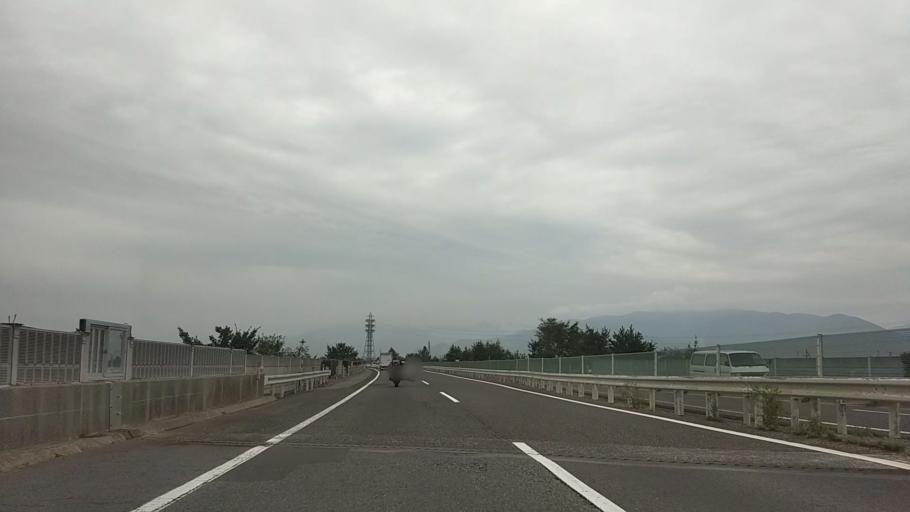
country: JP
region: Nagano
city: Matsumoto
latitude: 36.2214
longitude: 137.9340
